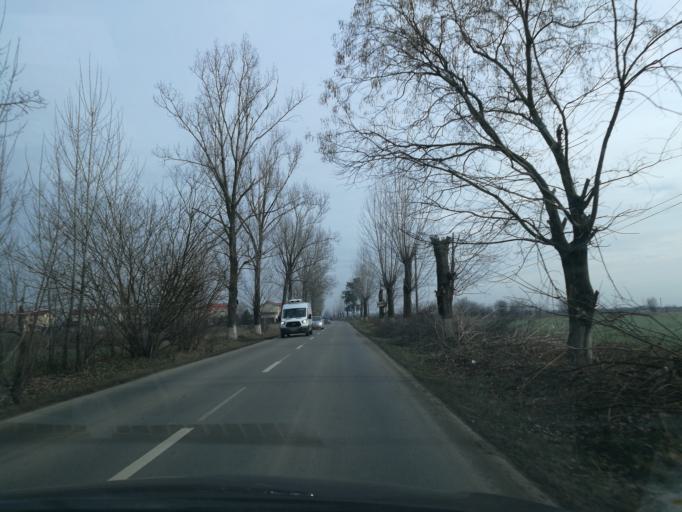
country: RO
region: Ilfov
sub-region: Comuna Balotesti
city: Balotesti
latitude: 44.6235
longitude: 26.1381
